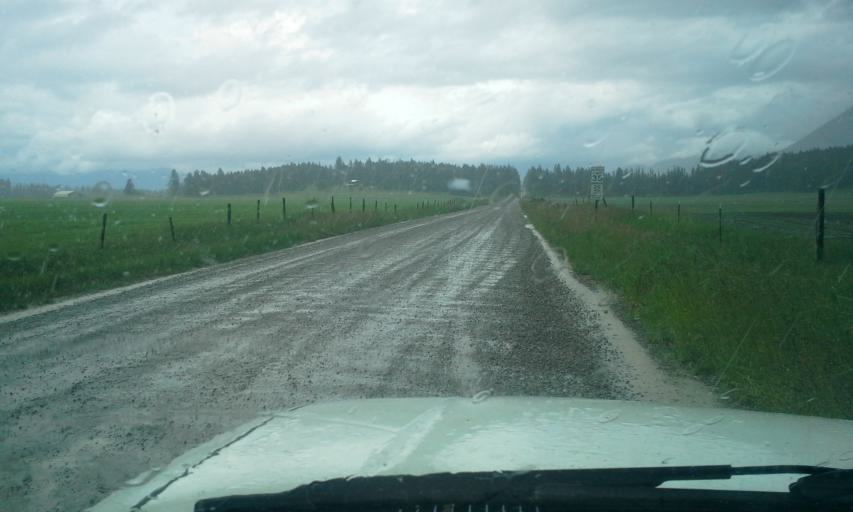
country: US
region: Montana
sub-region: Flathead County
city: Columbia Falls
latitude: 48.2691
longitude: -114.1435
